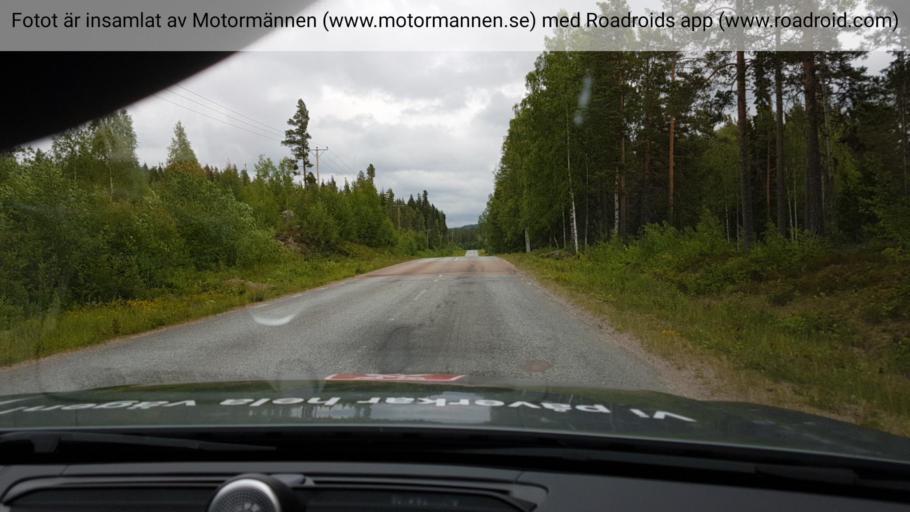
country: SE
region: Jaemtland
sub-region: Braecke Kommun
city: Braecke
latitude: 62.8724
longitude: 15.5861
